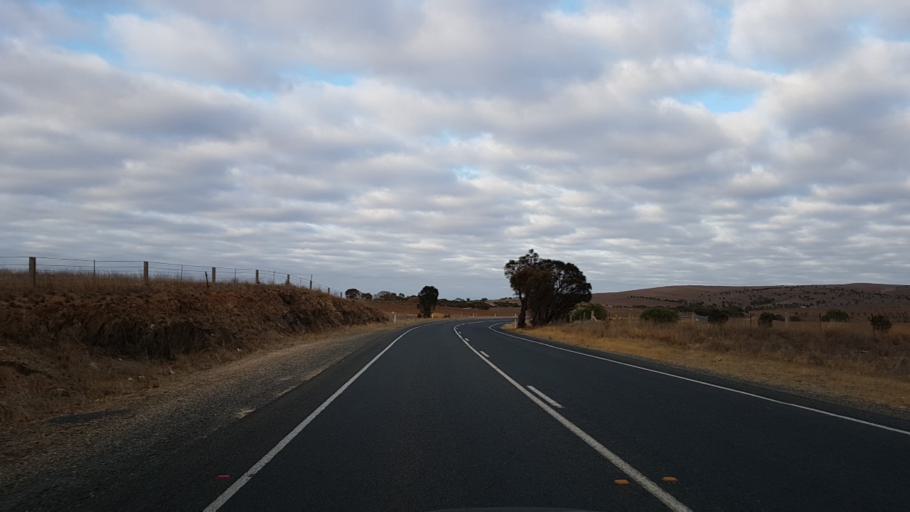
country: AU
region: South Australia
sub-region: Mount Barker
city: Callington
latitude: -35.1323
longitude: 139.0336
